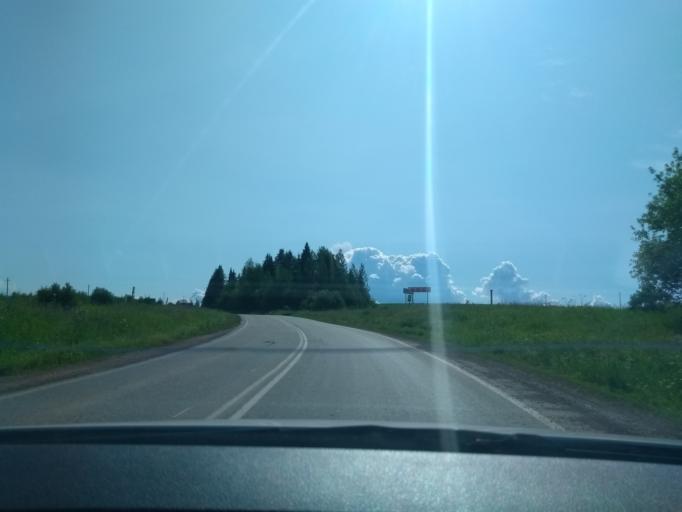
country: RU
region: Perm
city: Lobanovo
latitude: 57.8531
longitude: 56.3259
